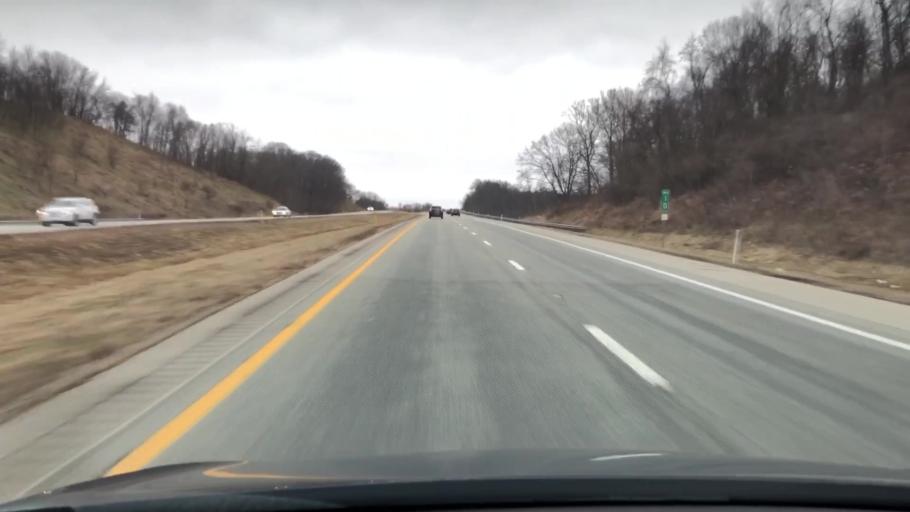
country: US
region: Pennsylvania
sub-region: Greene County
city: Morrisville
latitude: 39.8474
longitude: -80.1161
